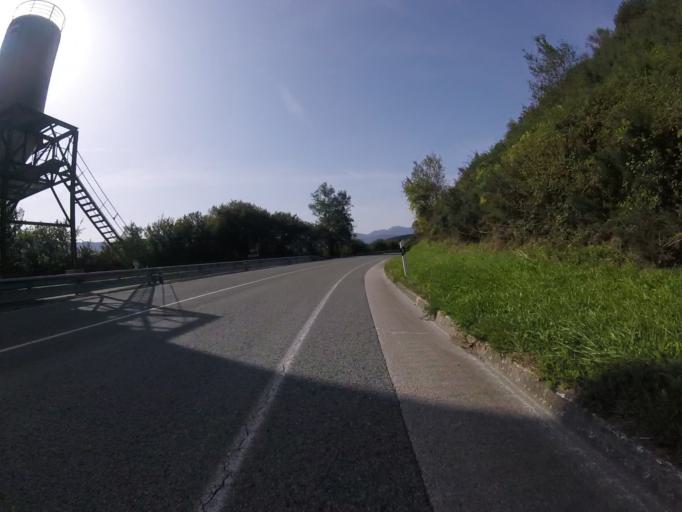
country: ES
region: Navarre
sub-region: Provincia de Navarra
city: Zugarramurdi
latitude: 43.1947
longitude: -1.4838
